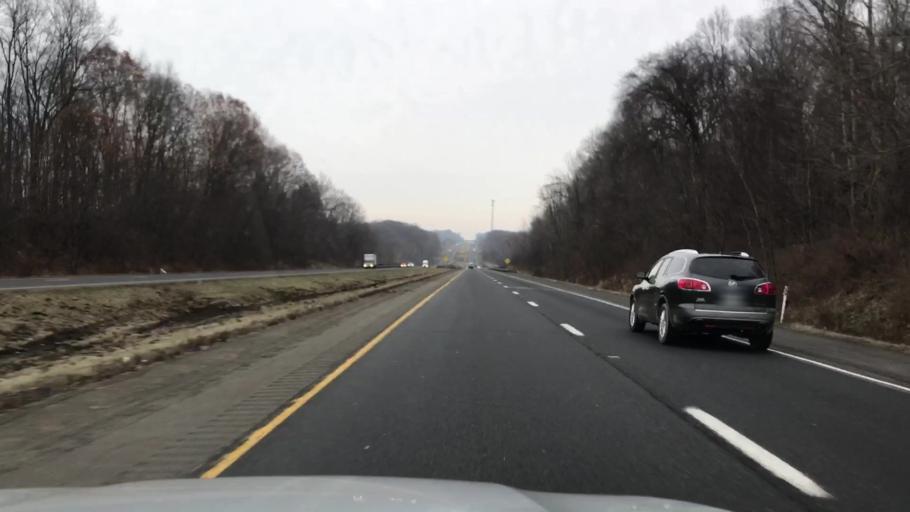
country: US
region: Pennsylvania
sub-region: Erie County
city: Girard
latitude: 41.9804
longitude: -80.2966
